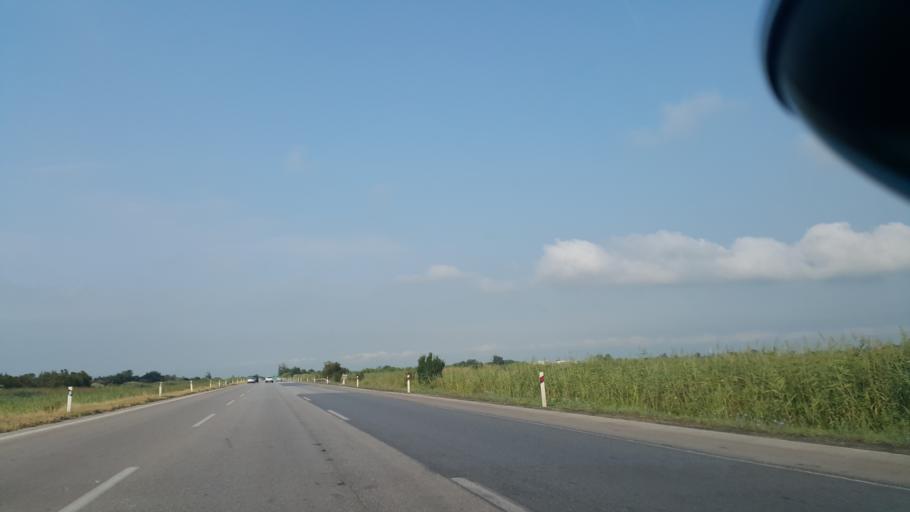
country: GR
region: Central Macedonia
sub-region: Nomos Thessalonikis
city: Sindos
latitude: 40.6329
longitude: 22.7795
